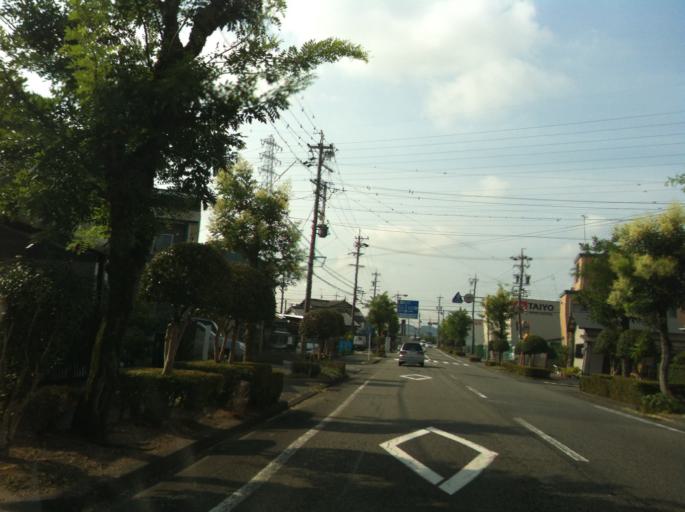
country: JP
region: Shizuoka
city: Shimada
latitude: 34.8403
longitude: 138.1680
